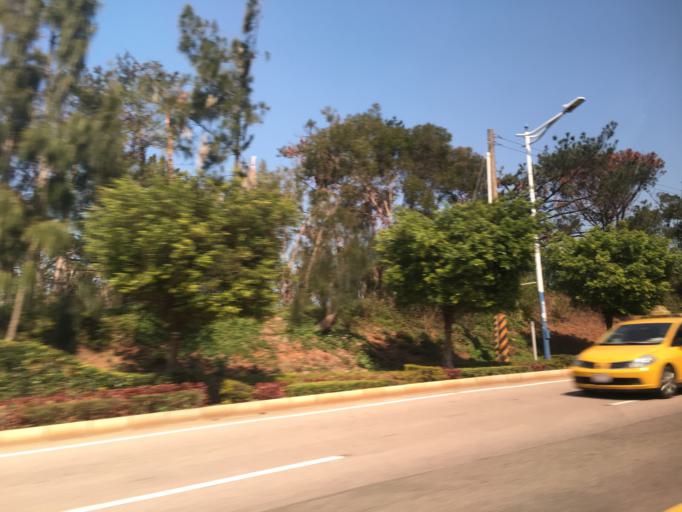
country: TW
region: Fukien
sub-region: Kinmen
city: Jincheng
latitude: 24.4356
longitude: 118.3505
